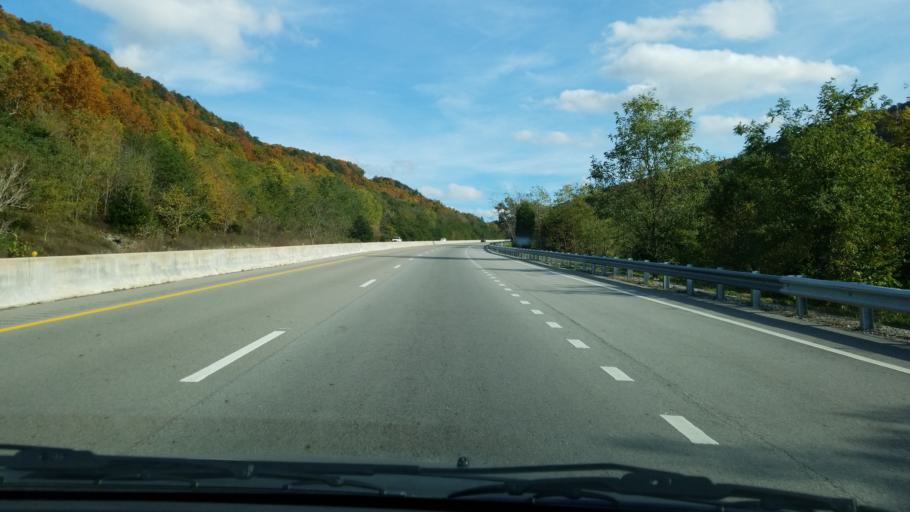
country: US
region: Tennessee
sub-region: Sequatchie County
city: Dunlap
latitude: 35.3619
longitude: -85.3242
